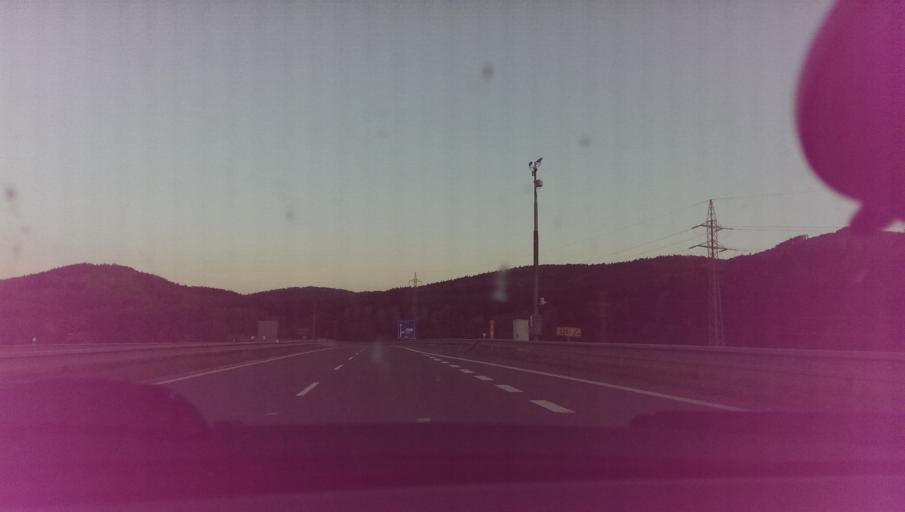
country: CZ
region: Zlin
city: Jablunka
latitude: 49.3683
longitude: 17.9447
